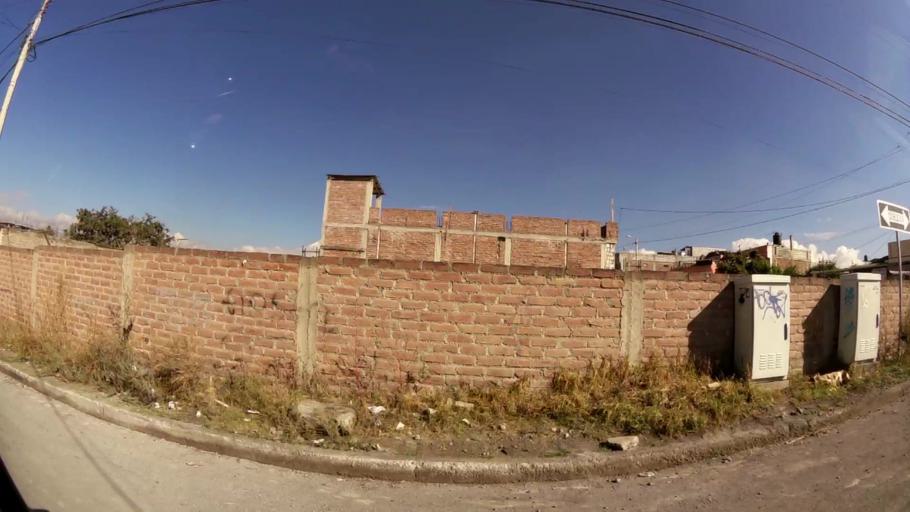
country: EC
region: Chimborazo
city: Riobamba
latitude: -1.6509
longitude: -78.6724
